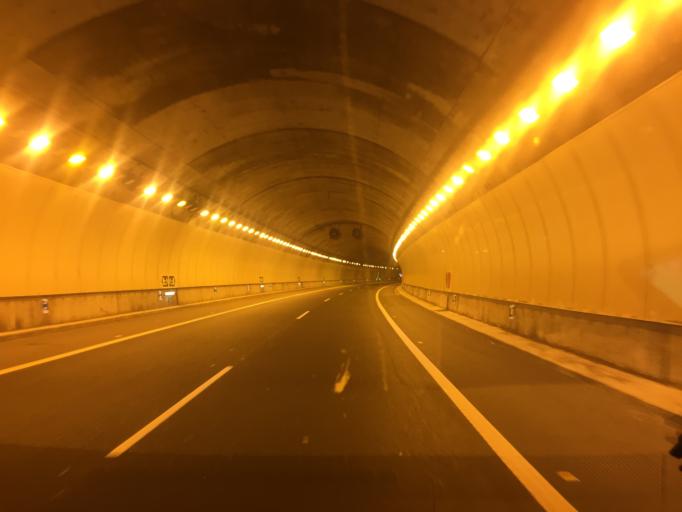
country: ES
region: Andalusia
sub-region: Provincia de Malaga
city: Nerja
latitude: 36.7672
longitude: -3.8734
